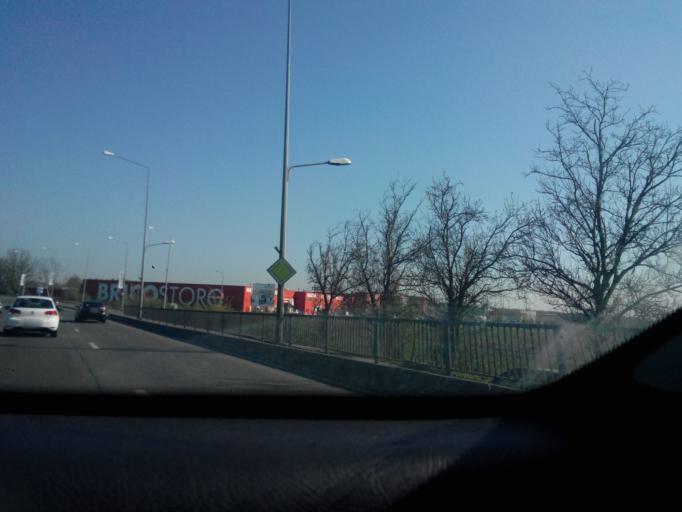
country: RO
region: Ilfov
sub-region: Comuna Otopeni
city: Otopeni
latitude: 44.5075
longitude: 26.0821
